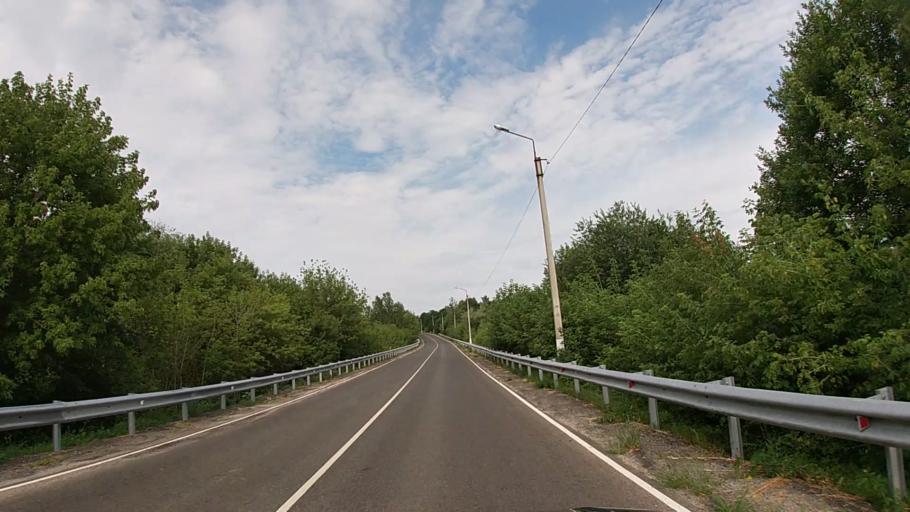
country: UA
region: Sumy
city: Krasnopillya
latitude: 50.8140
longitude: 35.4271
